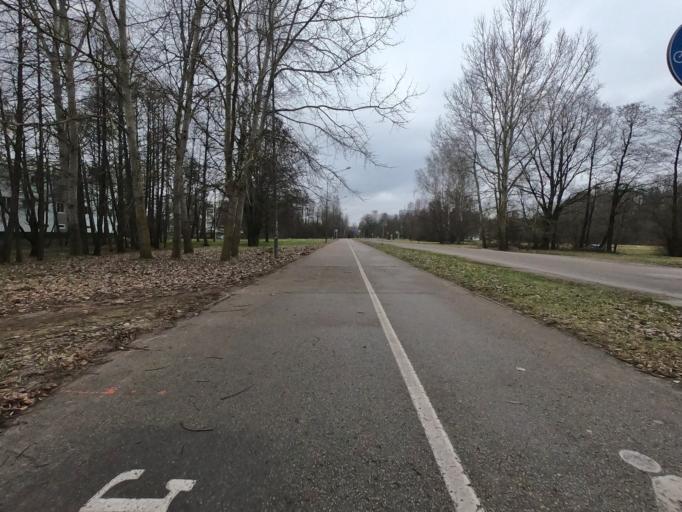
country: LV
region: Marupe
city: Marupe
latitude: 56.9512
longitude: 24.0091
